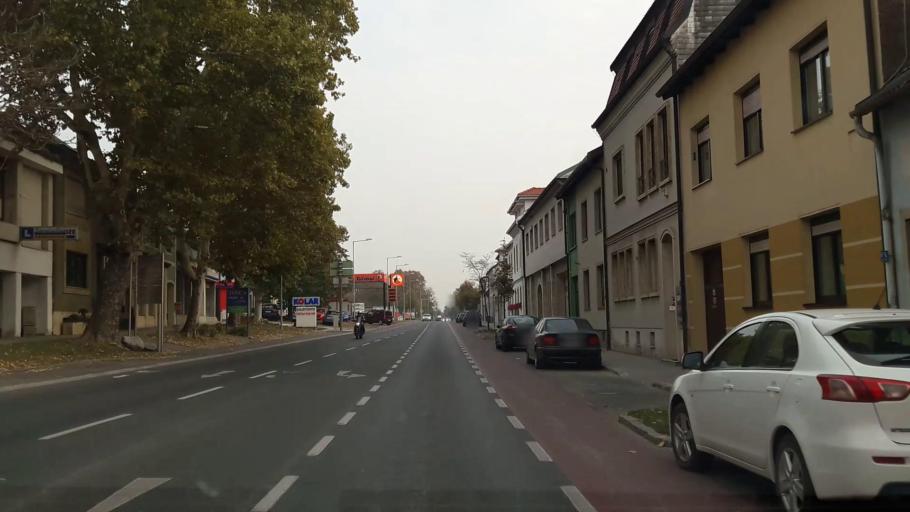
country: AT
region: Burgenland
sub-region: Politischer Bezirk Neusiedl am See
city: Neusiedl am See
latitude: 47.9440
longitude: 16.8493
